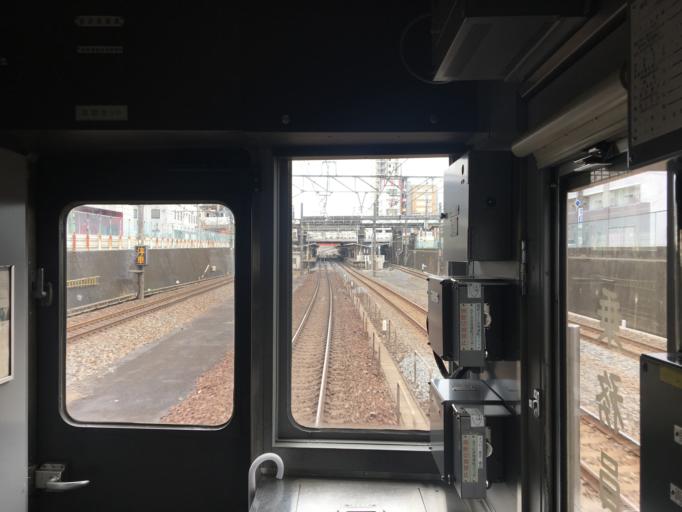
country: JP
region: Saitama
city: Shiki
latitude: 35.8174
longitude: 139.5829
